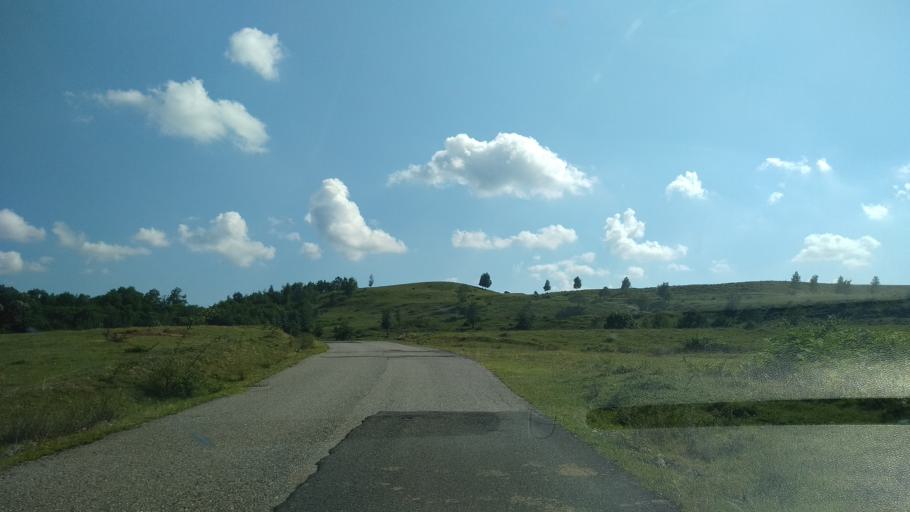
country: RO
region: Hunedoara
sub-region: Comuna Orastioara de Sus
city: Orastioara de Sus
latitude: 45.7180
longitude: 23.1598
